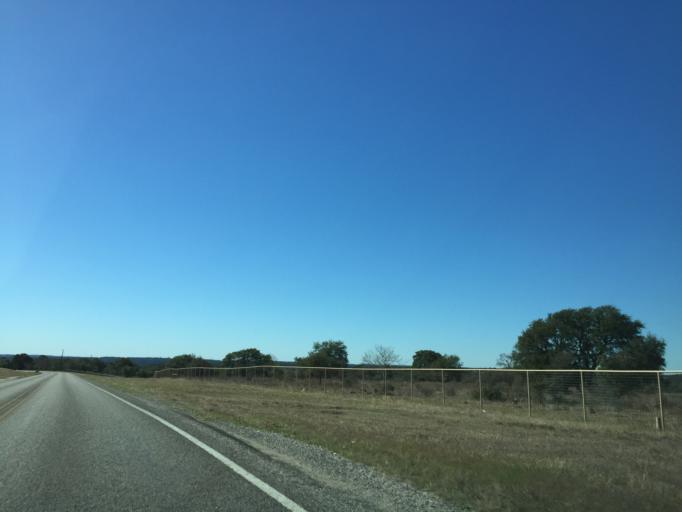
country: US
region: Texas
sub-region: Comal County
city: Canyon Lake
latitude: 29.7626
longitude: -98.3049
